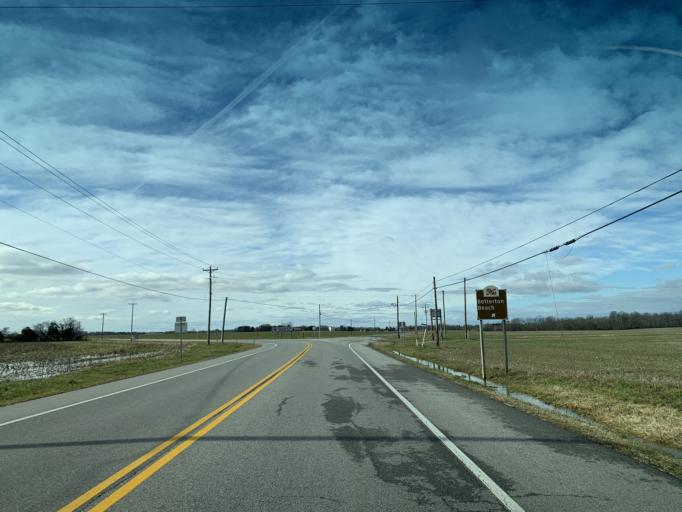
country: US
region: Maryland
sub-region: Queen Anne's County
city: Kingstown
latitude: 39.3233
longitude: -76.0227
